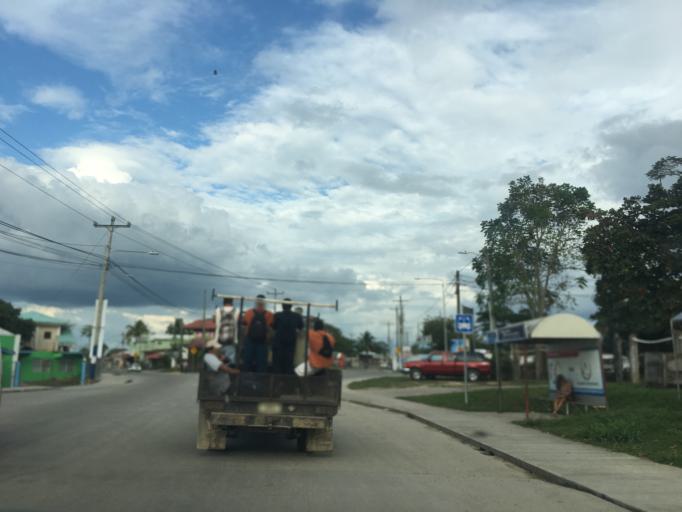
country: BZ
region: Cayo
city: San Ignacio
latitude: 17.1503
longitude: -89.0754
